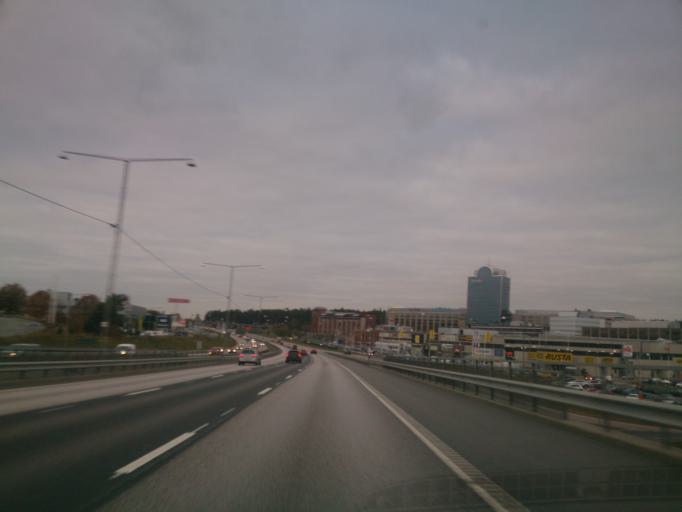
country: SE
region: Stockholm
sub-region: Upplands Vasby Kommun
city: Upplands Vaesby
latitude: 59.4953
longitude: 17.9227
